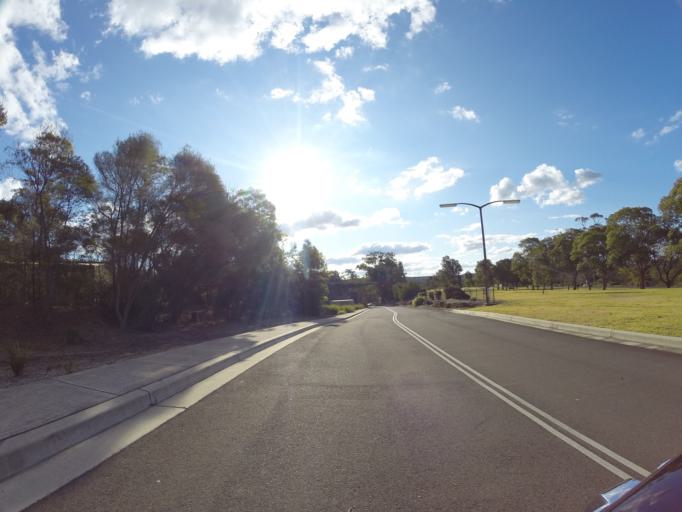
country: AU
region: New South Wales
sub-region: Penrith Municipality
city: Mulgoa
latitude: -33.8890
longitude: 150.5994
